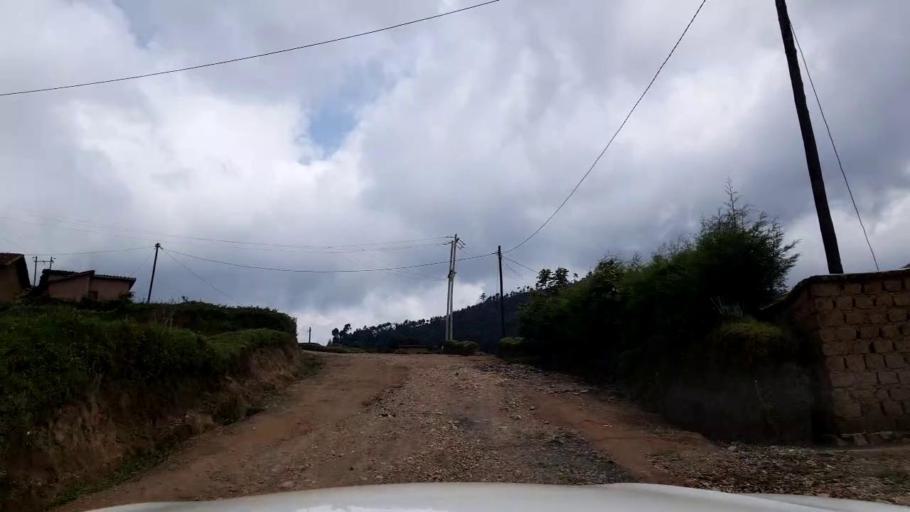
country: RW
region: Western Province
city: Kibuye
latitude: -1.9522
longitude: 29.4738
